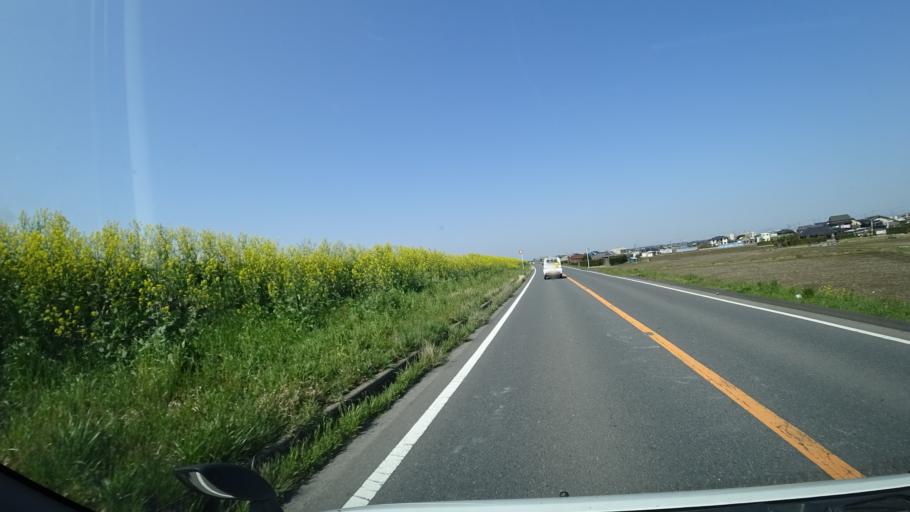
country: JP
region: Chiba
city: Katori-shi
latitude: 35.9198
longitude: 140.4679
